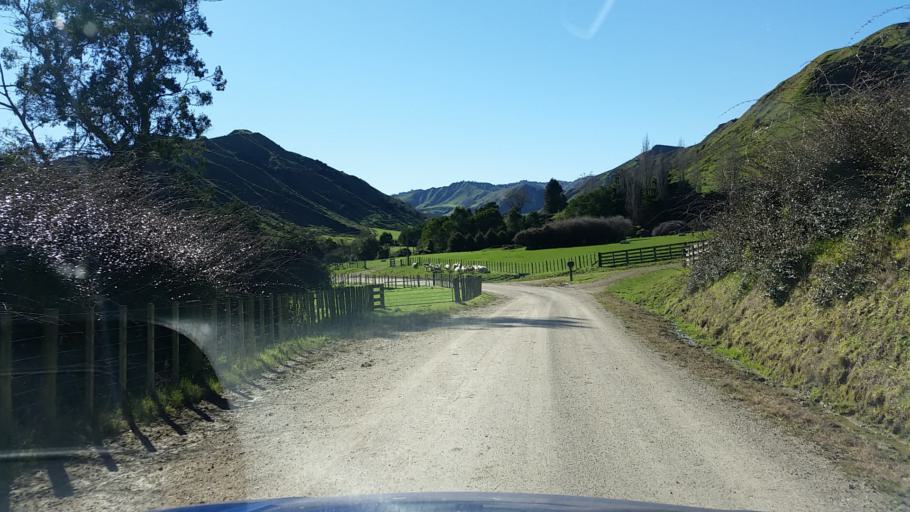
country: NZ
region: Manawatu-Wanganui
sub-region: Wanganui District
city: Wanganui
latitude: -39.5445
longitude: 174.9020
